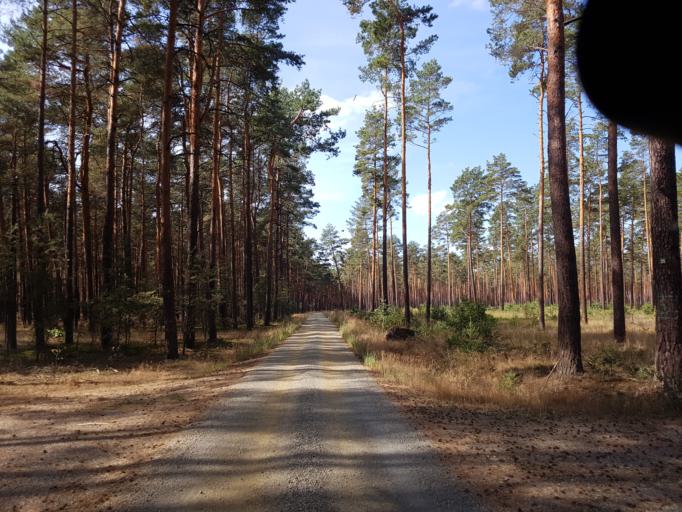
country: DE
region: Brandenburg
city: Sonnewalde
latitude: 51.7607
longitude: 13.6543
